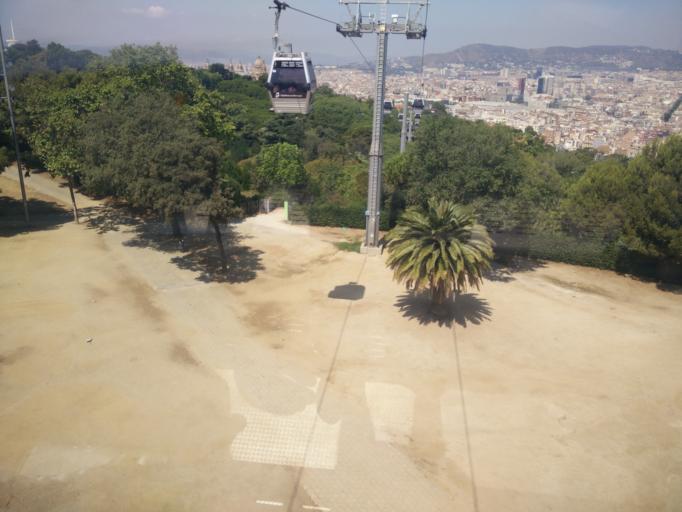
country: ES
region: Catalonia
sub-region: Provincia de Barcelona
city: Sants-Montjuic
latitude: 41.3677
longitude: 2.1674
